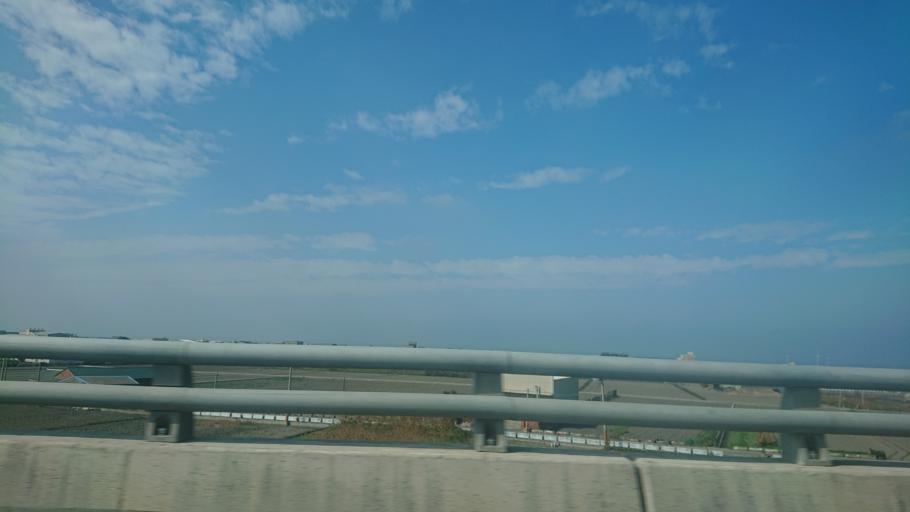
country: TW
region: Taiwan
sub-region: Changhua
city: Chang-hua
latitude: 24.0473
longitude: 120.4066
